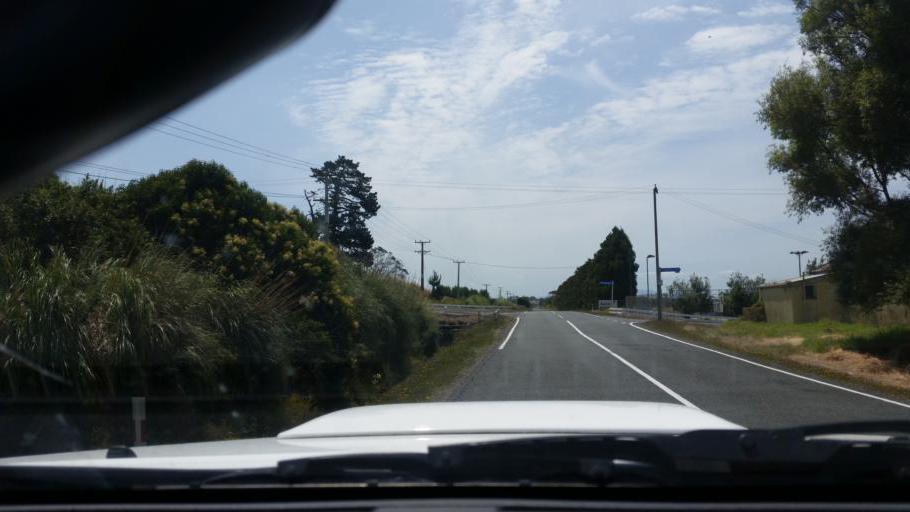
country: NZ
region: Northland
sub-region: Kaipara District
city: Dargaville
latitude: -36.0602
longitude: 173.9357
